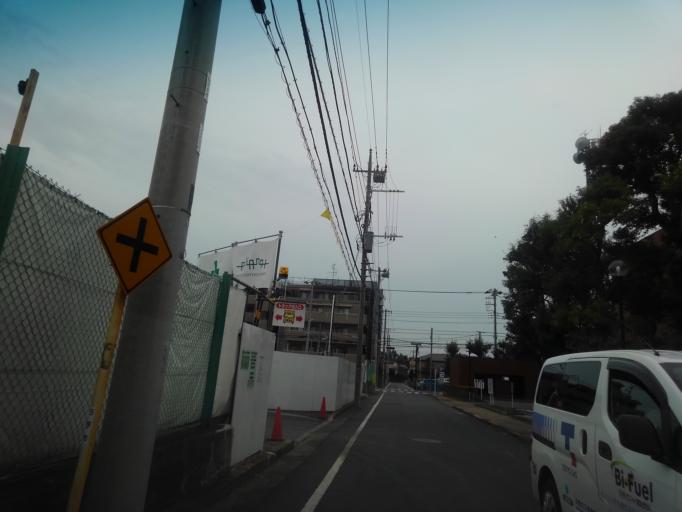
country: JP
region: Tokyo
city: Hino
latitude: 35.6709
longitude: 139.3958
